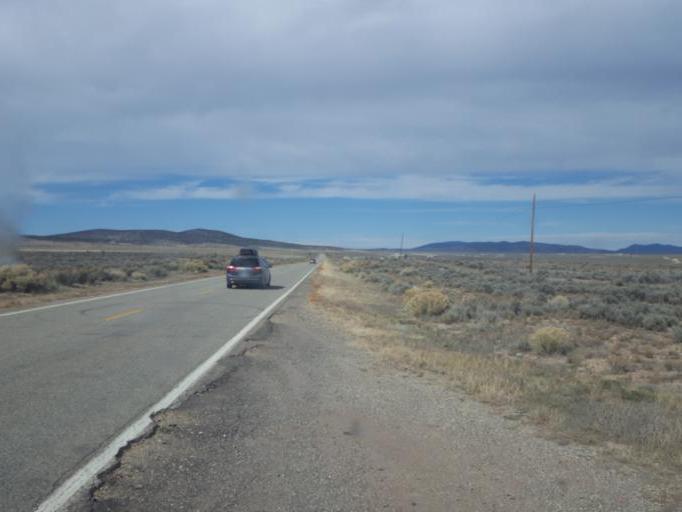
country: US
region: New Mexico
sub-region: Taos County
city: Arroyo Seco
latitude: 36.4893
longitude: -105.7510
